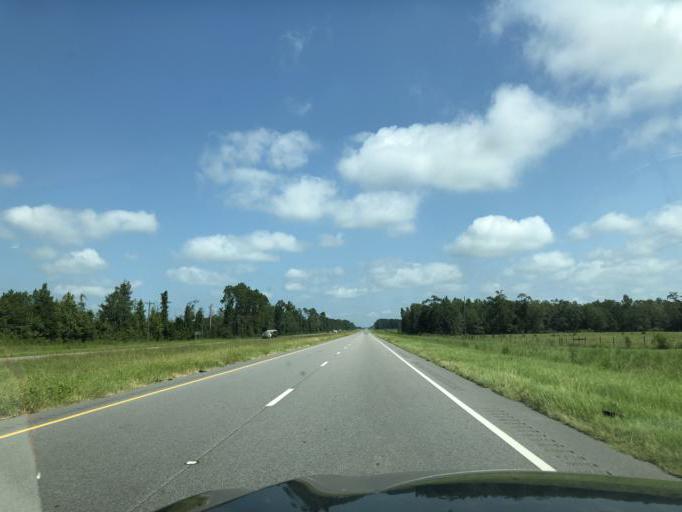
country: US
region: Alabama
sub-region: Houston County
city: Cottonwood
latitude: 31.0264
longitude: -85.4069
